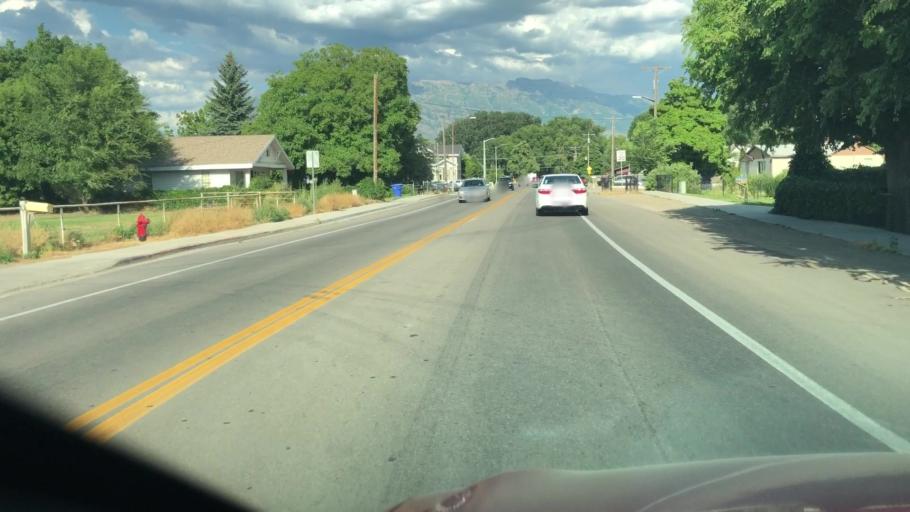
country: US
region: Utah
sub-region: Utah County
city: Lehi
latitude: 40.3872
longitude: -111.8603
